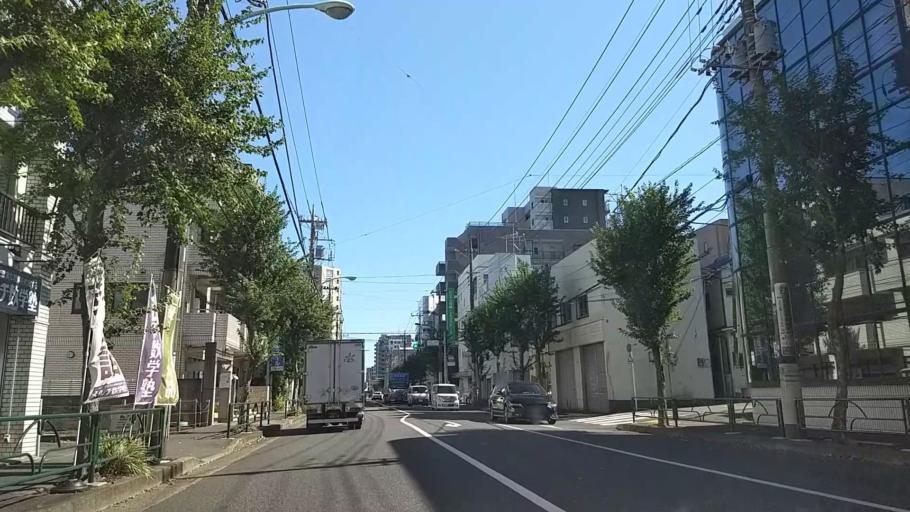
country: JP
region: Tokyo
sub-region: Machida-shi
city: Machida
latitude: 35.5514
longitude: 139.4450
